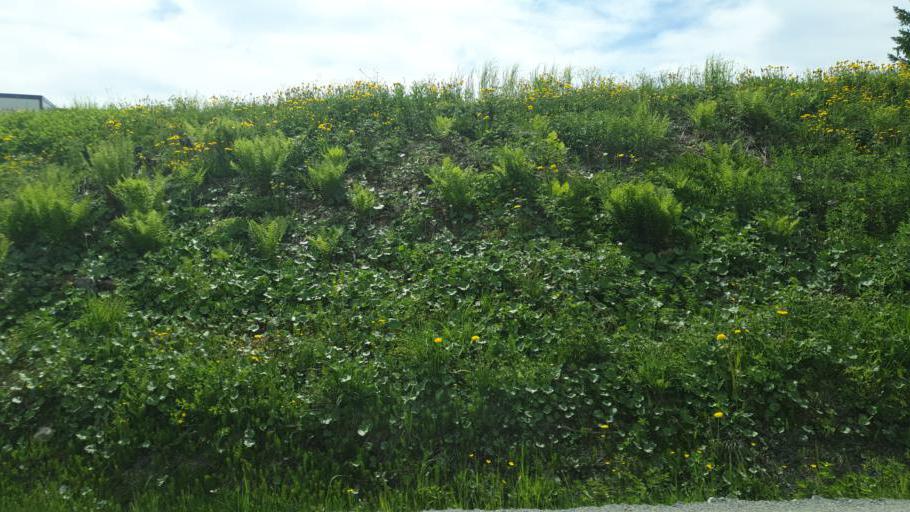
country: NO
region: Nord-Trondelag
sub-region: Leksvik
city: Leksvik
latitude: 63.6839
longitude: 10.5901
